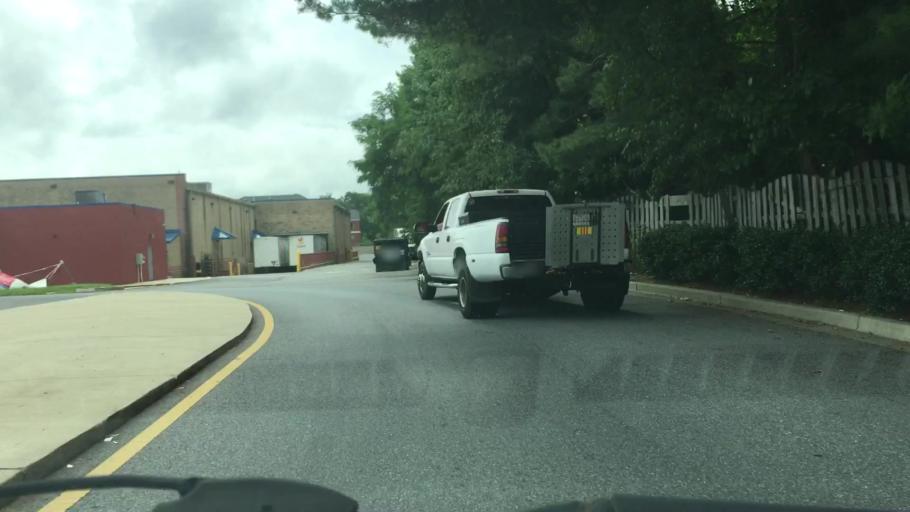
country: US
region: Maryland
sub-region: Prince George's County
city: Glenn Dale
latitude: 38.9897
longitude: -76.8242
